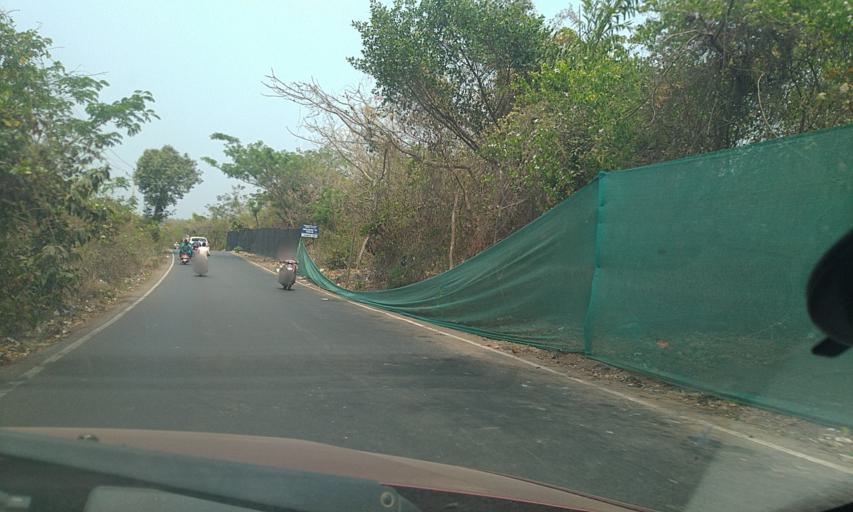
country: IN
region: Goa
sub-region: North Goa
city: Mapuca
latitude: 15.6121
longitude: 73.7950
